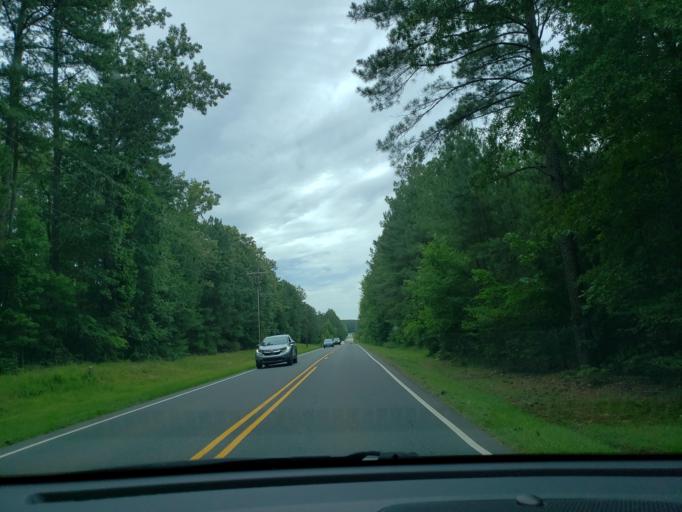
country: US
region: North Carolina
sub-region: Orange County
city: Chapel Hill
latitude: 35.8573
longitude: -79.0144
